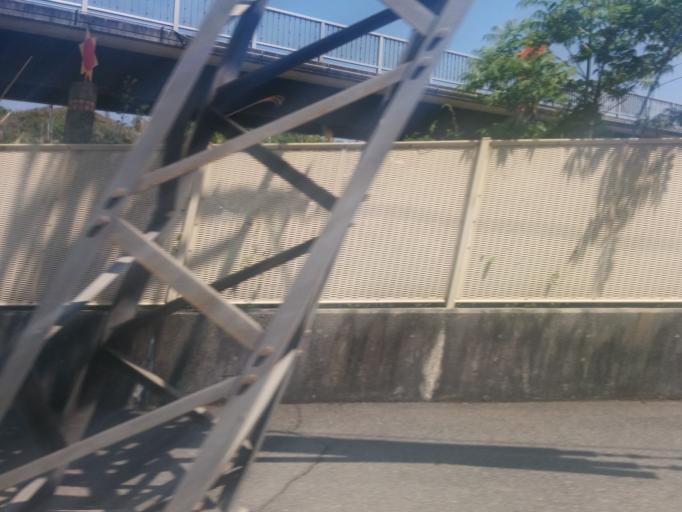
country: JP
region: Osaka
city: Kashihara
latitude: 34.5554
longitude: 135.6453
